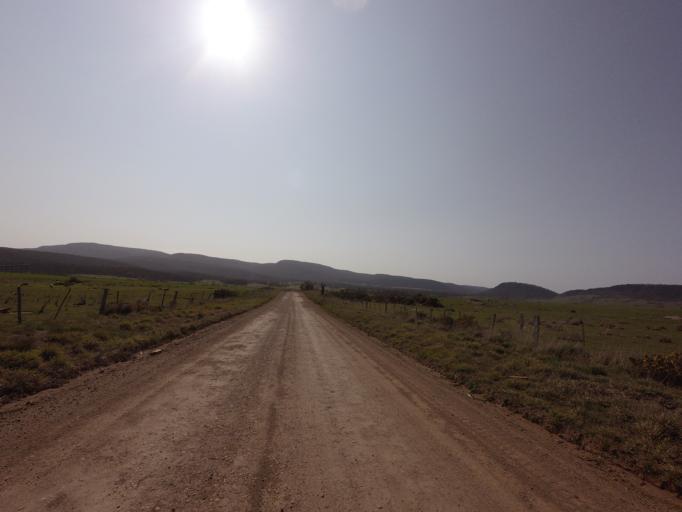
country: AU
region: Tasmania
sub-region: Break O'Day
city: St Helens
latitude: -41.8231
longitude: 147.9349
